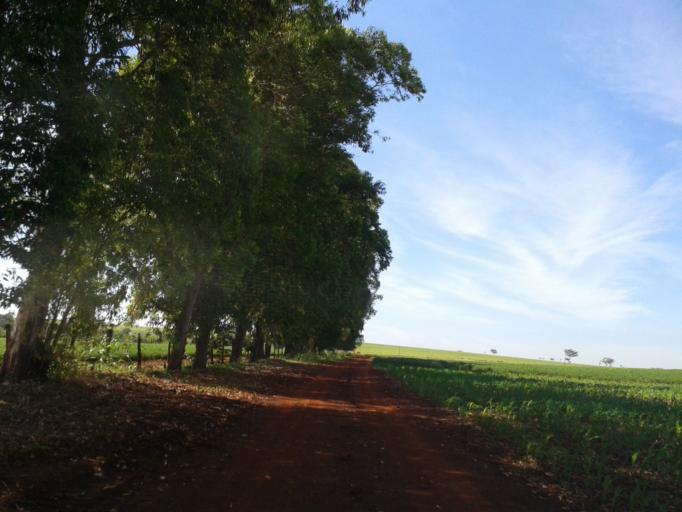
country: BR
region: Minas Gerais
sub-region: Capinopolis
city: Capinopolis
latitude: -18.6317
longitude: -49.7317
